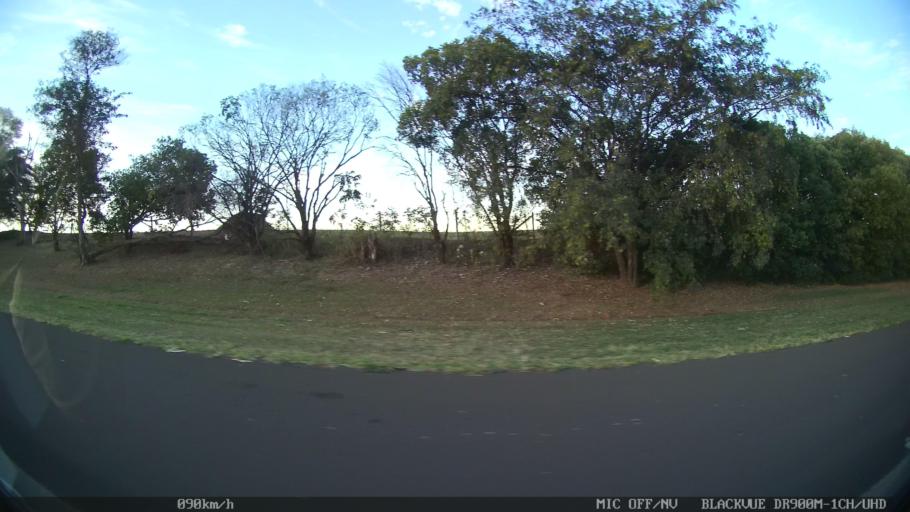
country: BR
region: Sao Paulo
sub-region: Pindorama
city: Pindorama
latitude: -21.1909
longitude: -48.9500
